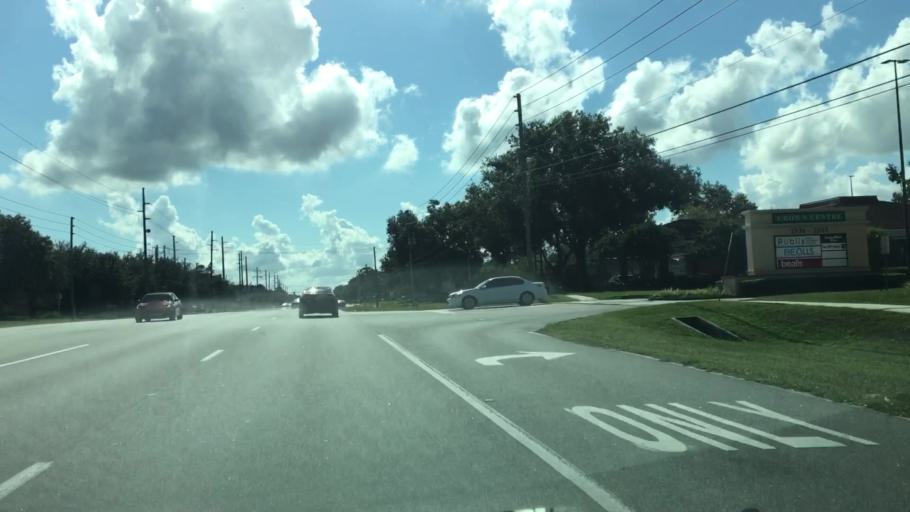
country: US
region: Florida
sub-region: Volusia County
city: Deltona
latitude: 28.9152
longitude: -81.2941
